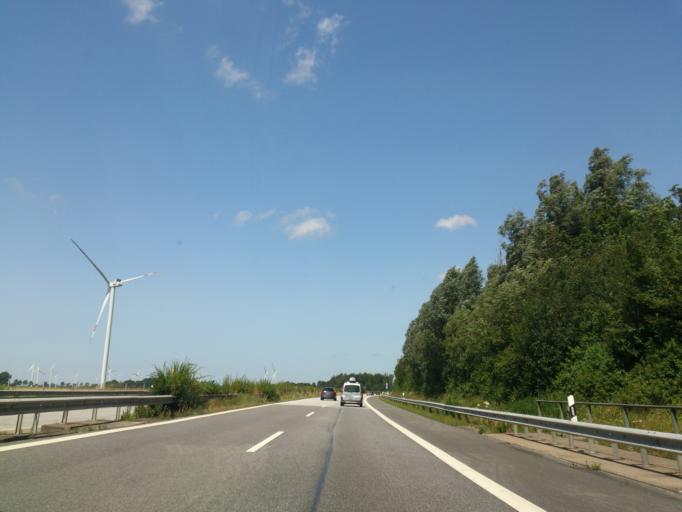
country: DE
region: Schleswig-Holstein
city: Lohe-Rickelshof
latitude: 54.1821
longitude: 9.0521
